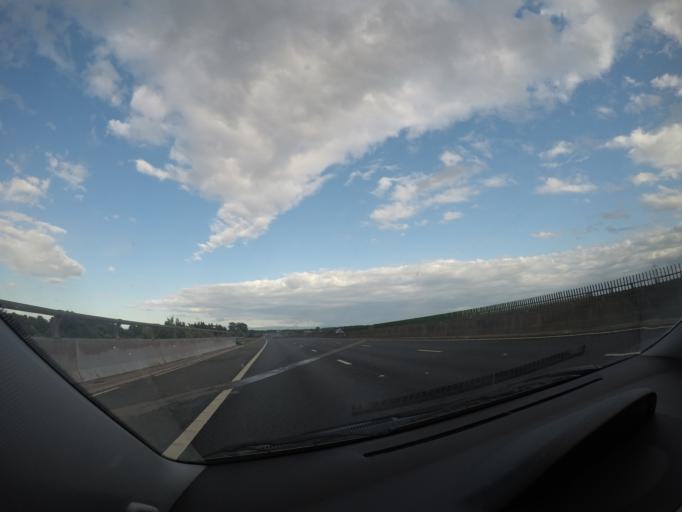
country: GB
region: Scotland
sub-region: Dumfries and Galloway
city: Gretna
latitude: 54.9801
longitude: -3.0233
